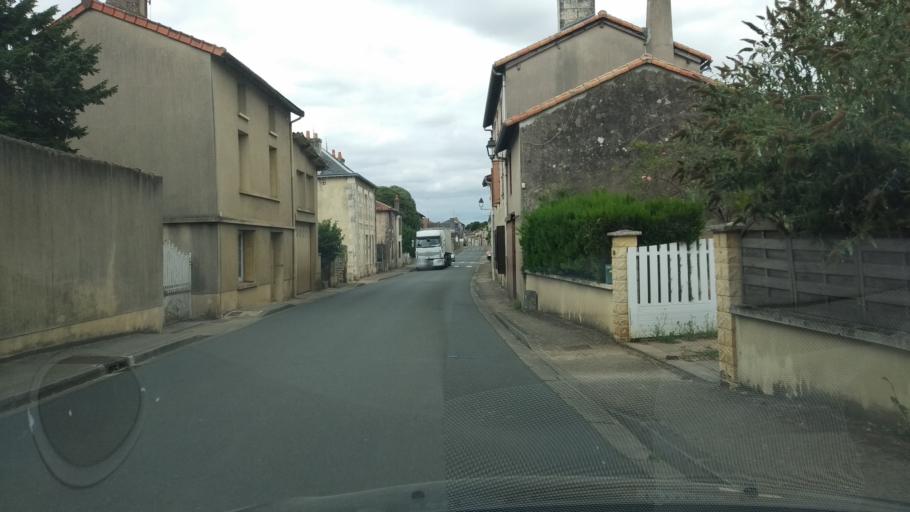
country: FR
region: Poitou-Charentes
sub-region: Departement de la Vienne
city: La Villedieu-du-Clain
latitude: 46.4537
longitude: 0.3670
